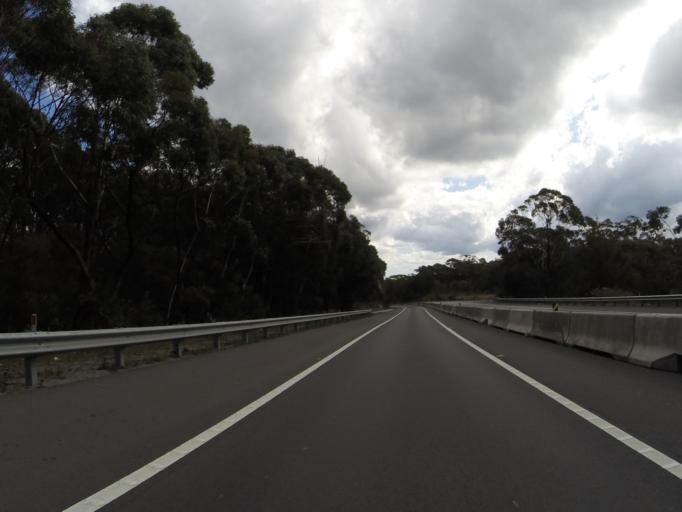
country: AU
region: New South Wales
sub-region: Wollongong
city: Mount Keira
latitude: -34.3530
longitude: 150.8070
